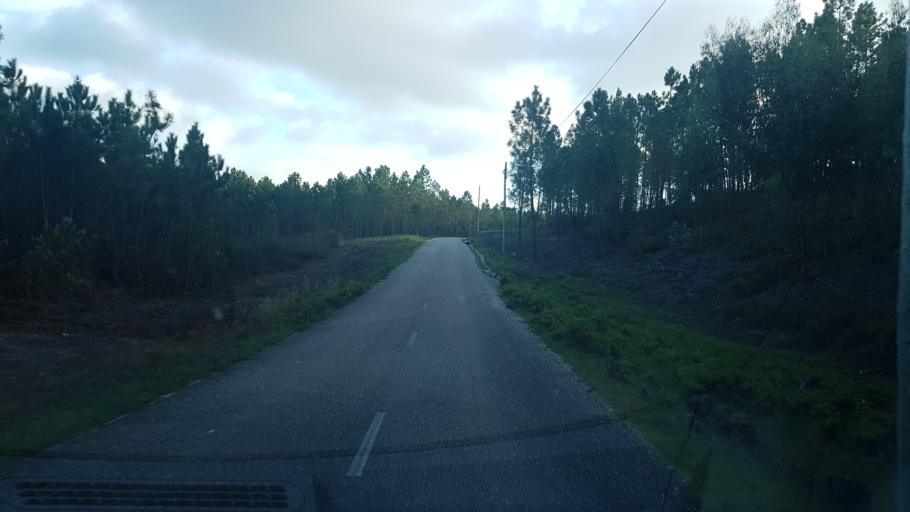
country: PT
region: Castelo Branco
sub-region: Vila de Rei
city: Vila de Rei
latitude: 39.5946
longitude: -8.1192
